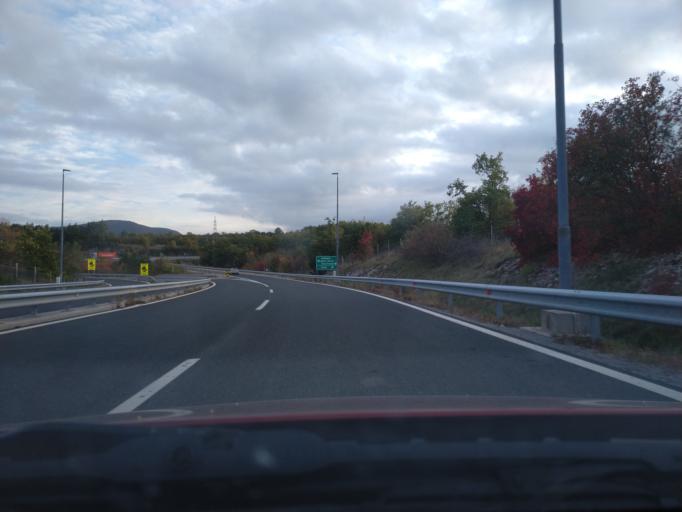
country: SI
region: Divaca
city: Divaca
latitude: 45.6691
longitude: 13.9664
